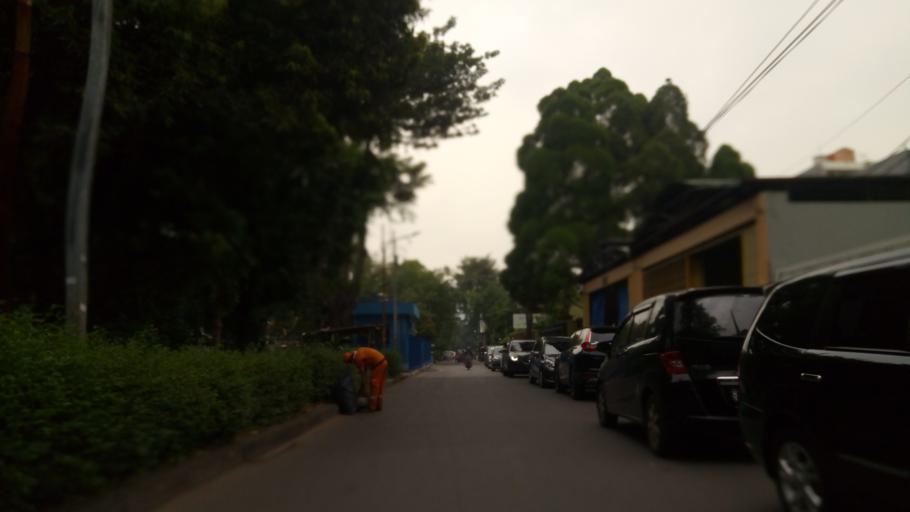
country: ID
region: Jakarta Raya
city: Jakarta
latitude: -6.1435
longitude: 106.8413
